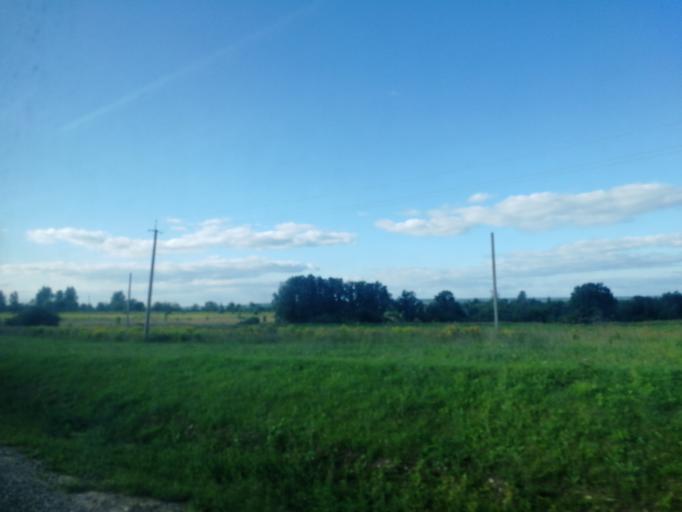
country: RU
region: Tula
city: Leninskiy
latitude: 54.2450
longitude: 37.3281
